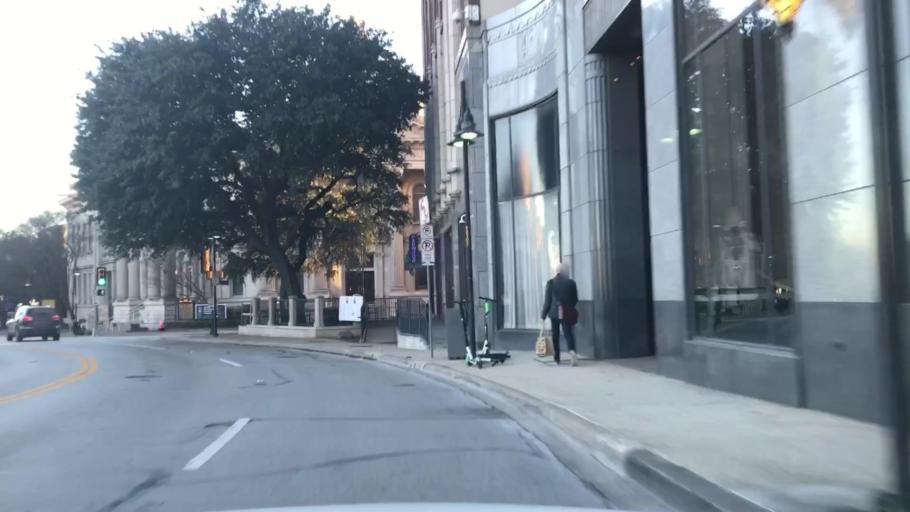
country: US
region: Texas
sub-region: Dallas County
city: Dallas
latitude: 32.7801
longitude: -96.7938
